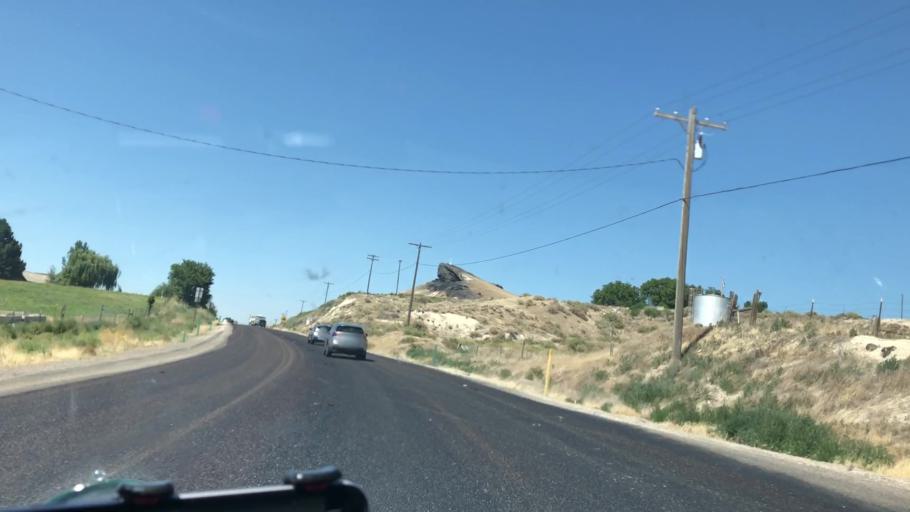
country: US
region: Idaho
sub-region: Owyhee County
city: Marsing
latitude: 43.5520
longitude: -116.7923
